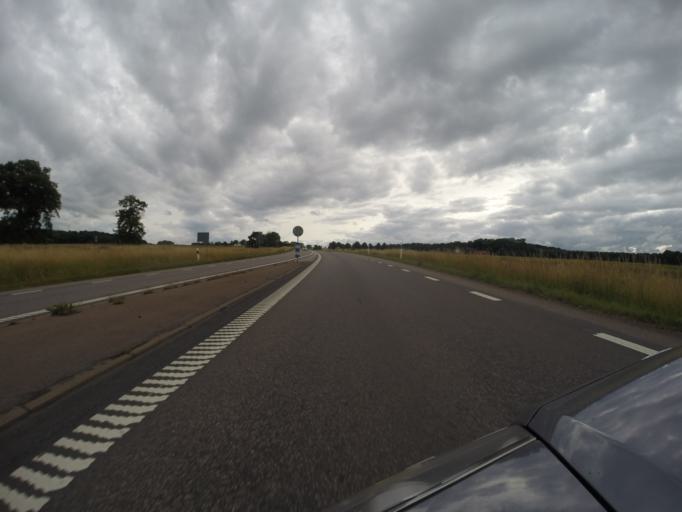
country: SE
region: Skane
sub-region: Helsingborg
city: Odakra
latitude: 56.0969
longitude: 12.7851
